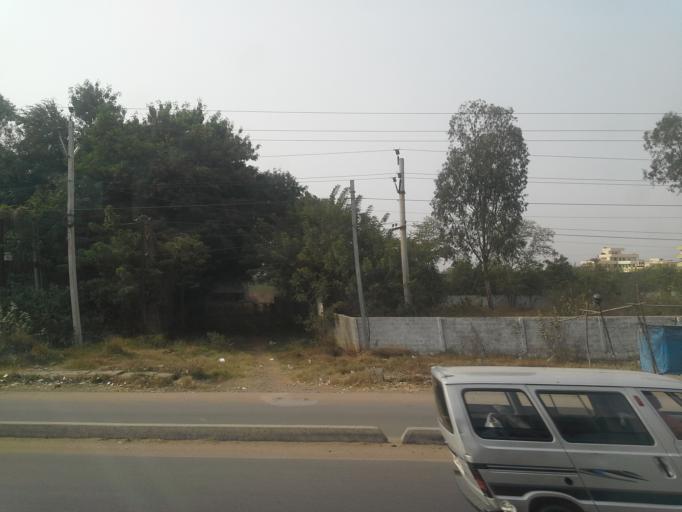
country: IN
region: Telangana
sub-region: Medak
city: Patancheru
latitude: 17.5252
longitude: 78.2712
